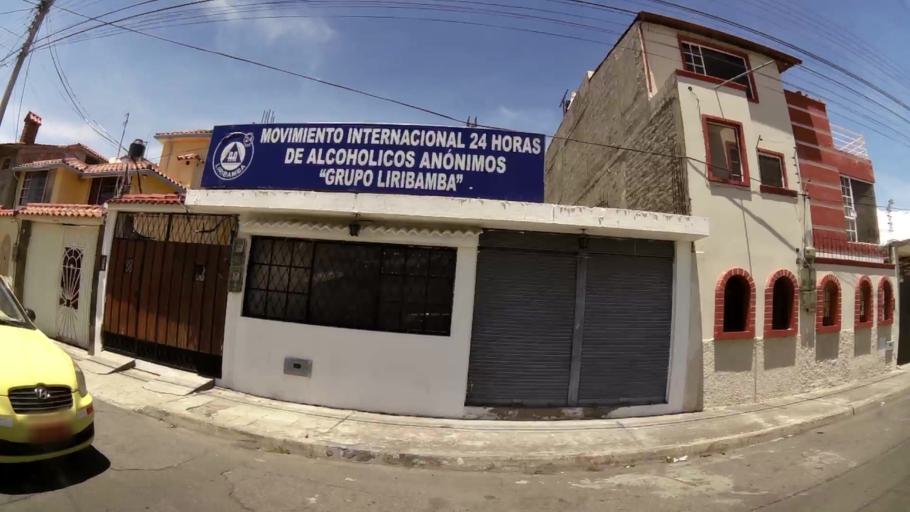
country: EC
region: Chimborazo
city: Riobamba
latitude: -1.6798
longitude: -78.6489
